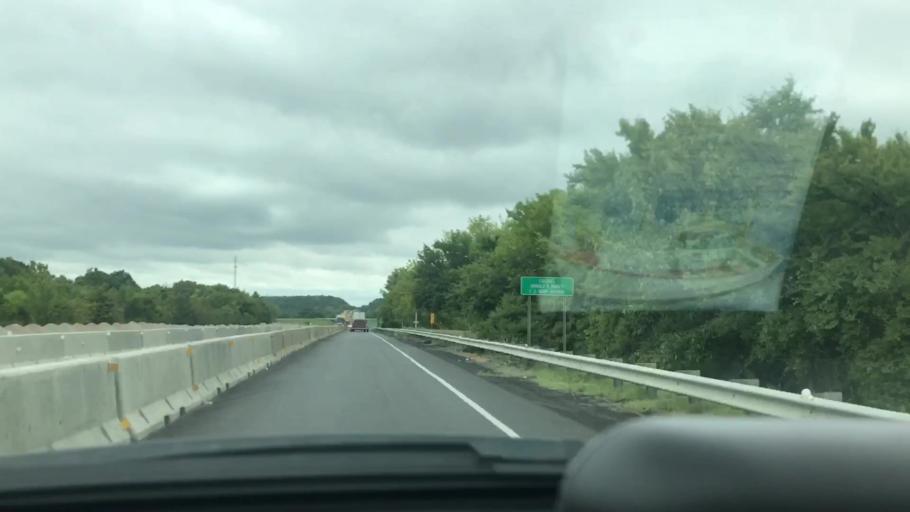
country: US
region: Oklahoma
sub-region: McIntosh County
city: Eufaula
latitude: 35.2544
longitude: -95.5862
